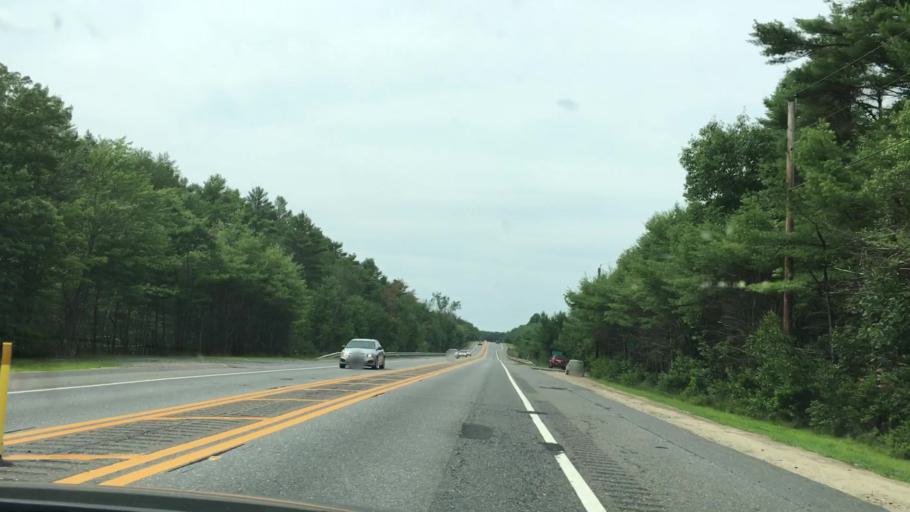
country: US
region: Massachusetts
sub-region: Worcester County
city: Gardner
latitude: 42.6081
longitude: -71.9949
